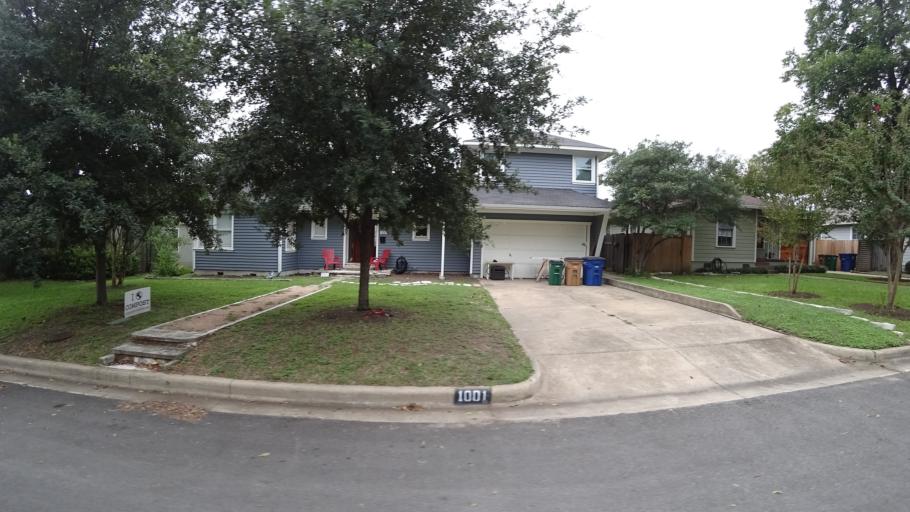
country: US
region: Texas
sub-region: Travis County
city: Austin
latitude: 30.3022
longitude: -97.7199
